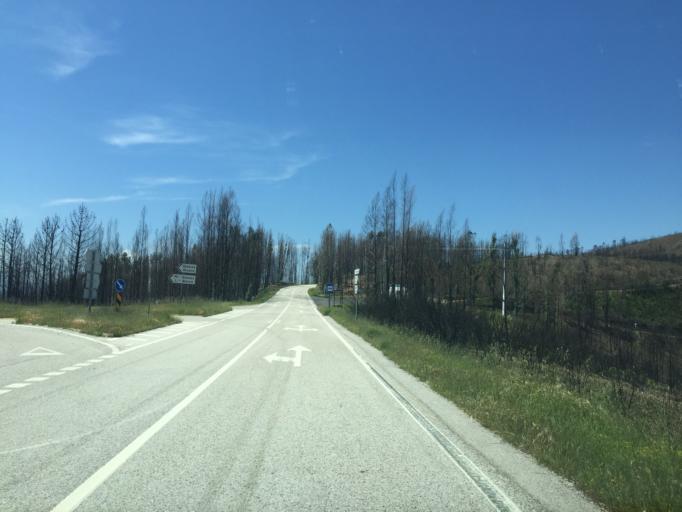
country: PT
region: Coimbra
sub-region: Pampilhosa da Serra
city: Pampilhosa da Serra
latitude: 40.0065
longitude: -7.9918
